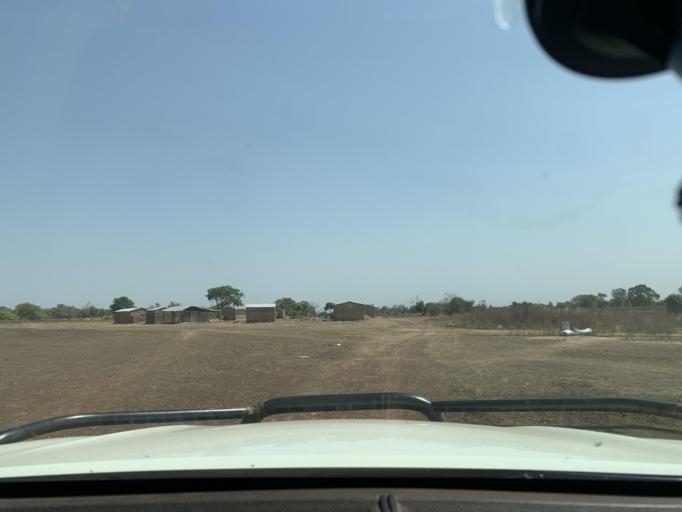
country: ML
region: Sikasso
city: Kolondieba
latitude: 10.8418
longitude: -6.8040
